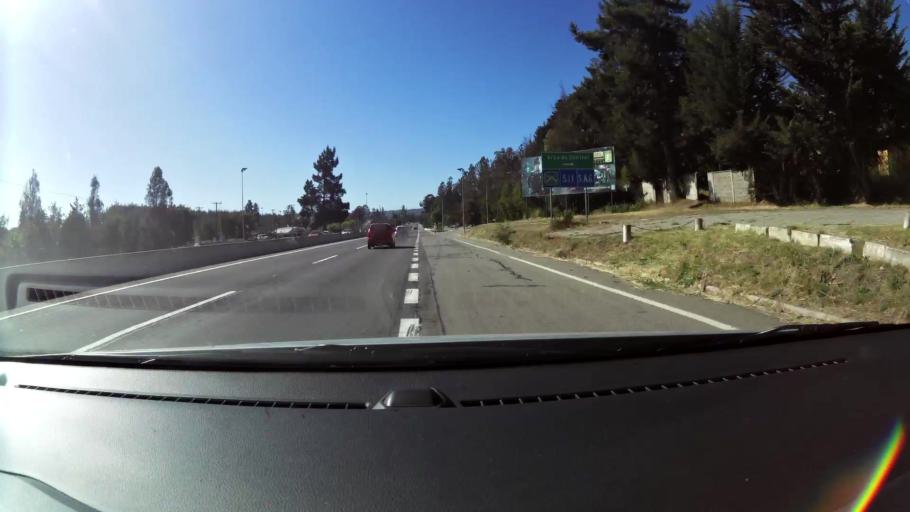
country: CL
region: Valparaiso
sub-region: Provincia de Valparaiso
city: Vina del Mar
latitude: -33.1481
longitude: -71.5591
